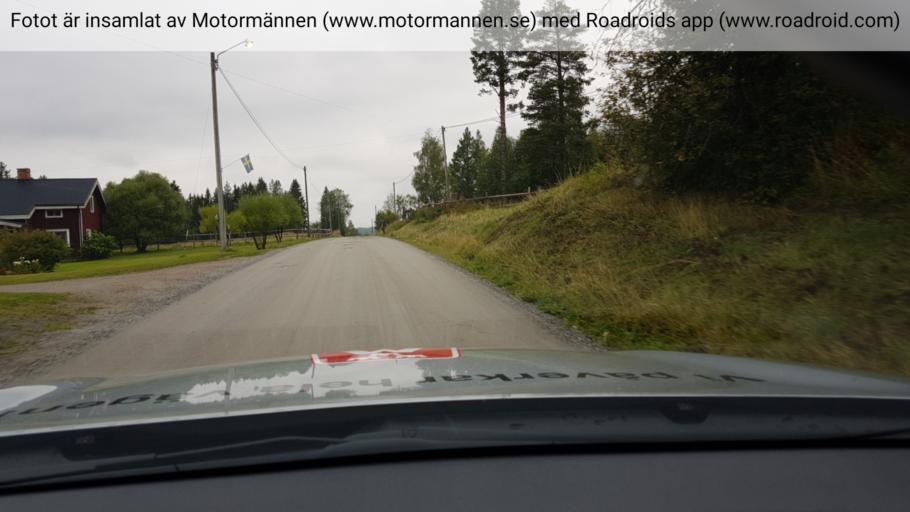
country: SE
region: Jaemtland
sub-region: Braecke Kommun
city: Braecke
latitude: 62.7705
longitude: 15.4854
